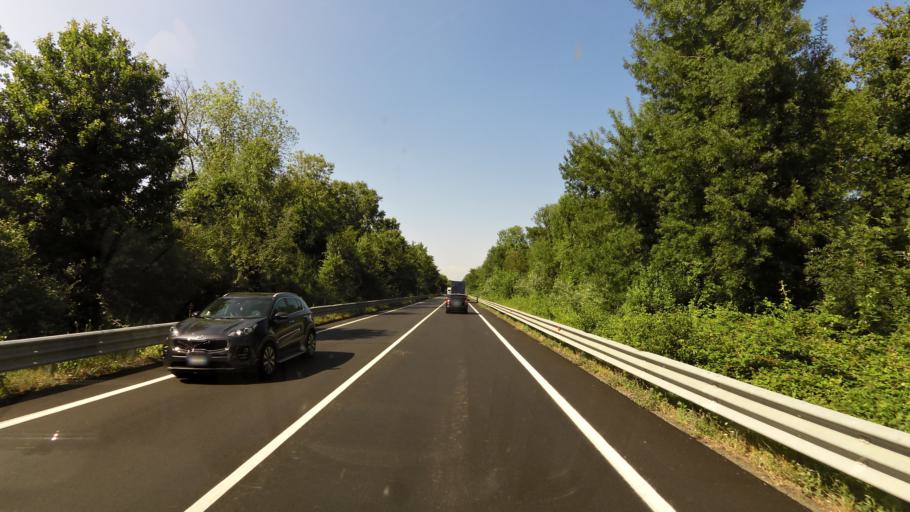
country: IT
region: Emilia-Romagna
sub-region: Provincia di Ravenna
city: Marina Romea
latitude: 44.5184
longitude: 12.2273
